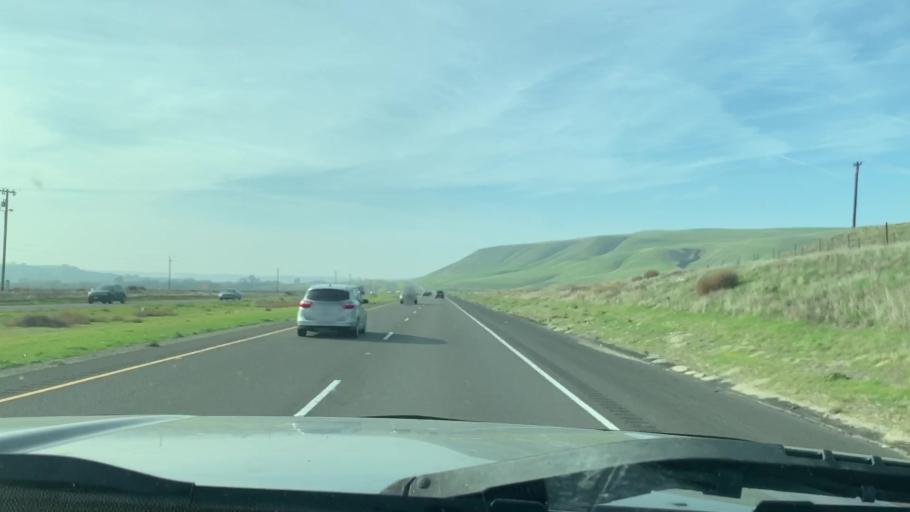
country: US
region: California
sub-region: San Luis Obispo County
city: Shandon
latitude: 35.6618
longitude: -120.4290
